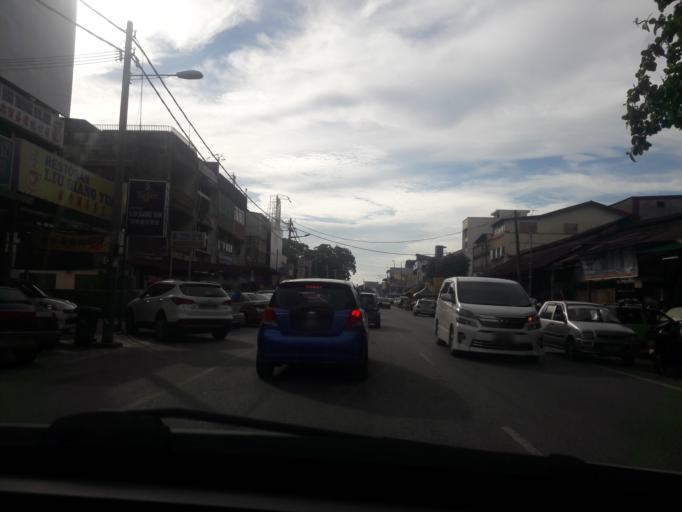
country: MY
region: Kedah
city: Sungai Petani
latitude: 5.6376
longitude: 100.4953
